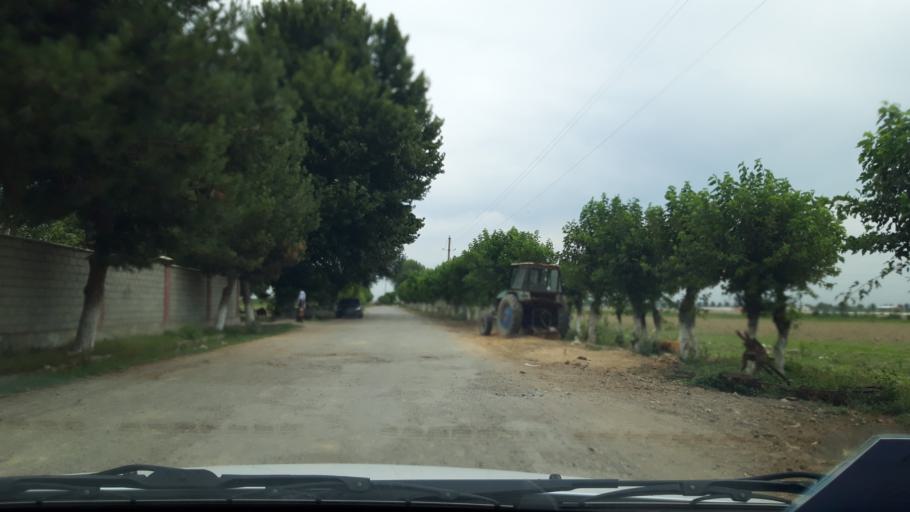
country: UZ
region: Namangan
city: Uychi
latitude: 41.0210
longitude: 71.9304
